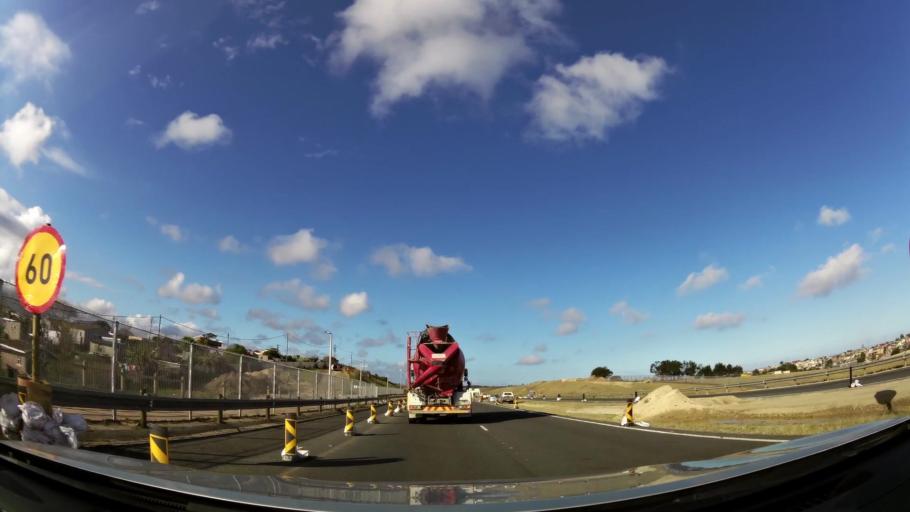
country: ZA
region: Western Cape
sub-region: Eden District Municipality
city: George
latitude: -33.9954
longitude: 22.4841
